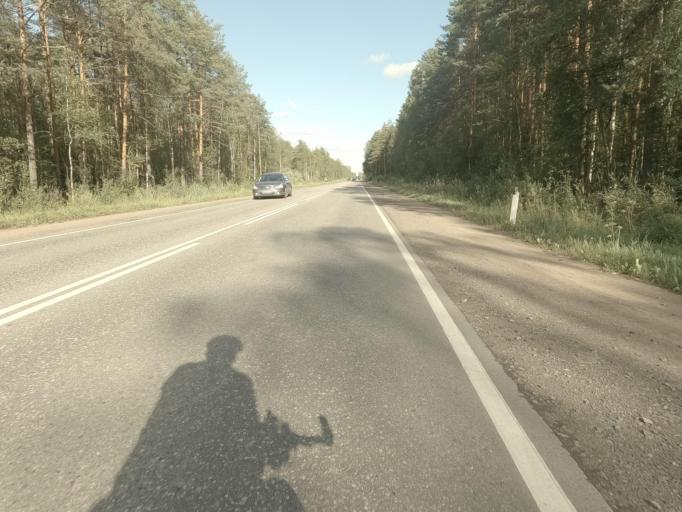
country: RU
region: Leningrad
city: Imeni Morozova
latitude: 59.9749
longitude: 30.9682
